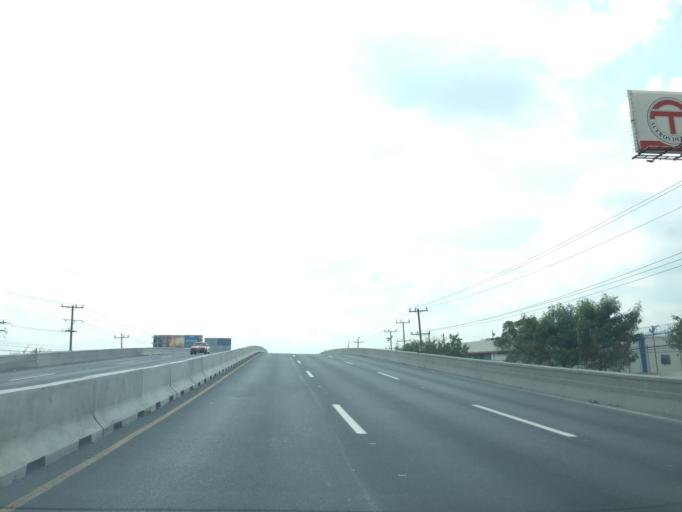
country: MX
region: Nuevo Leon
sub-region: Apodaca
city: Fraccionamiento Cosmopolis Octavo Sector
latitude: 25.8048
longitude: -100.2754
